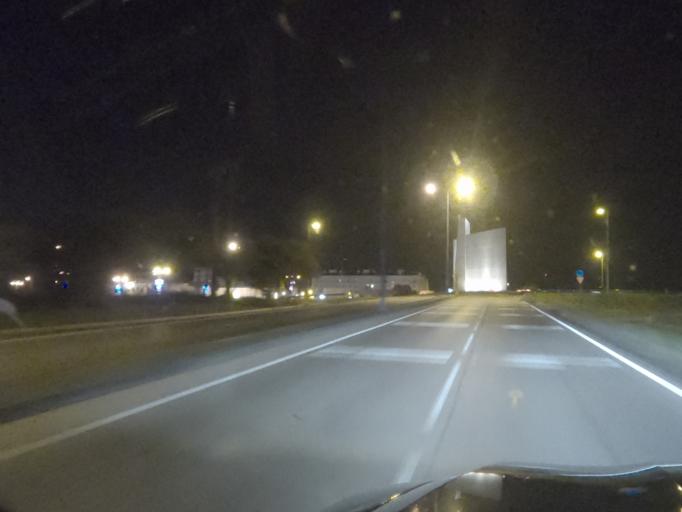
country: PT
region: Setubal
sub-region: Montijo
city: Montijo
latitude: 38.7009
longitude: -8.9445
